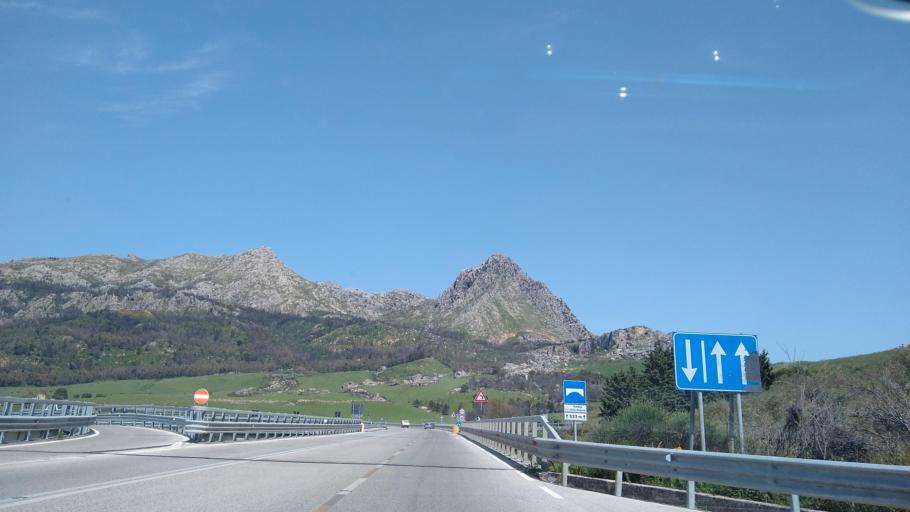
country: IT
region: Sicily
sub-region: Palermo
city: San Giuseppe Jato
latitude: 37.9817
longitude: 13.2328
